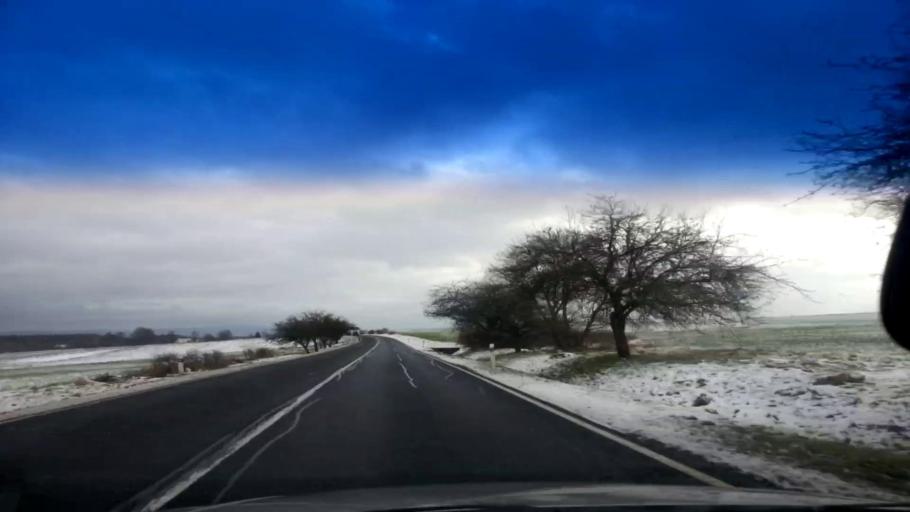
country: CZ
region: Karlovarsky
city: Hazlov
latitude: 50.1490
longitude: 12.2911
